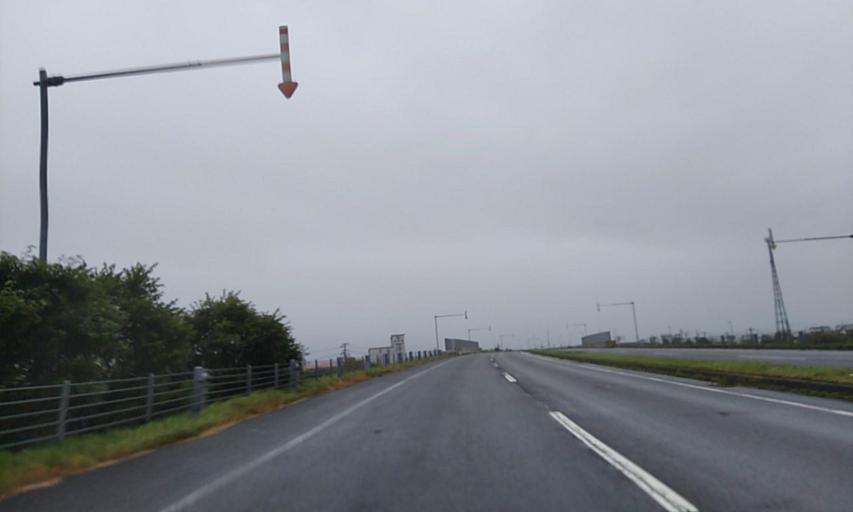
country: JP
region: Hokkaido
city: Kushiro
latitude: 43.0103
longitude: 144.2566
